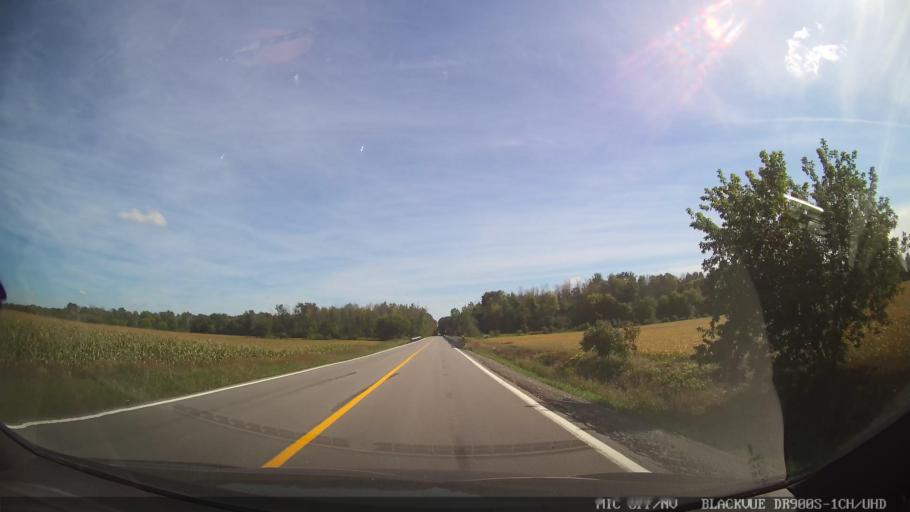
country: CA
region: Ontario
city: Bells Corners
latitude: 45.0928
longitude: -75.7037
